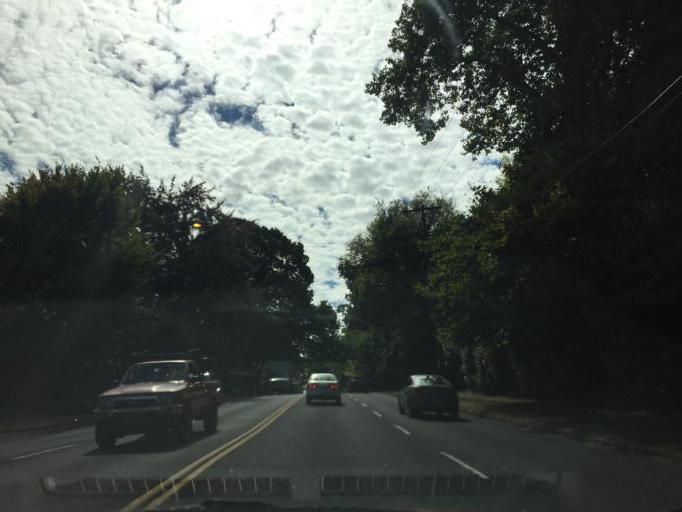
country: US
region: Oregon
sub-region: Multnomah County
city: Portland
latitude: 45.5209
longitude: -122.6231
